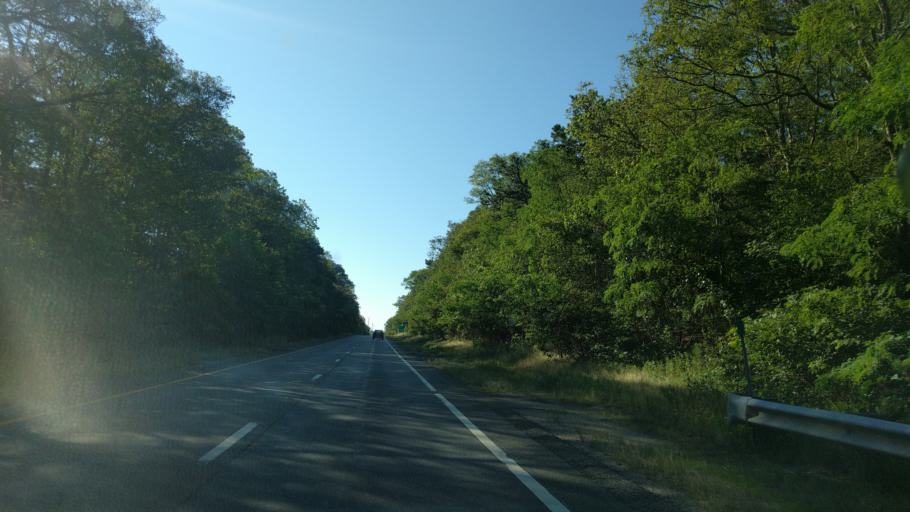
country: US
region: Massachusetts
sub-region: Barnstable County
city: West Barnstable
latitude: 41.6993
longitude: -70.3908
